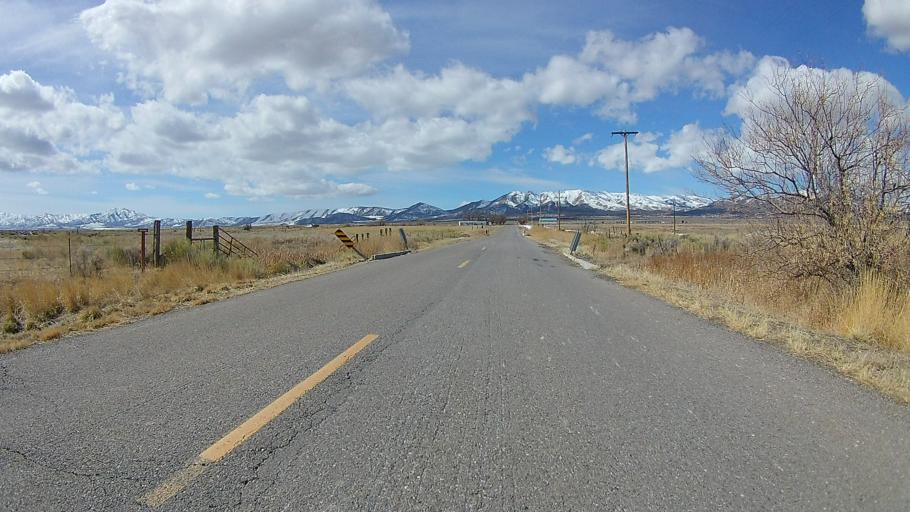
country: US
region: Utah
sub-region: Tooele County
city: Tooele
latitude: 40.1737
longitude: -112.4191
